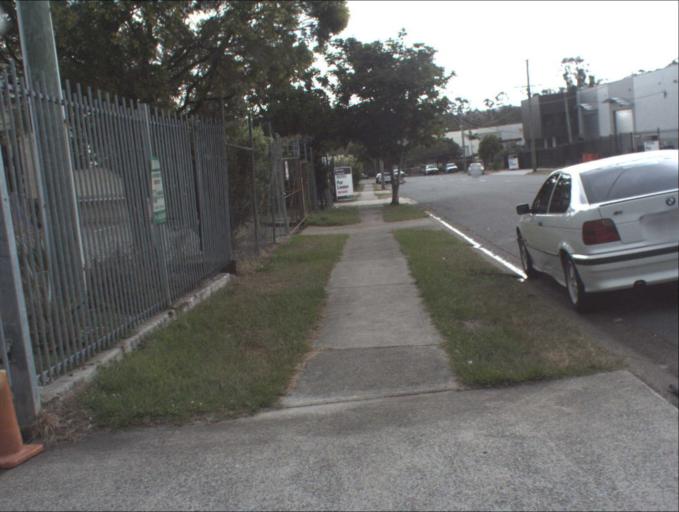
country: AU
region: Queensland
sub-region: Logan
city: Beenleigh
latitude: -27.6815
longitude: 153.1938
